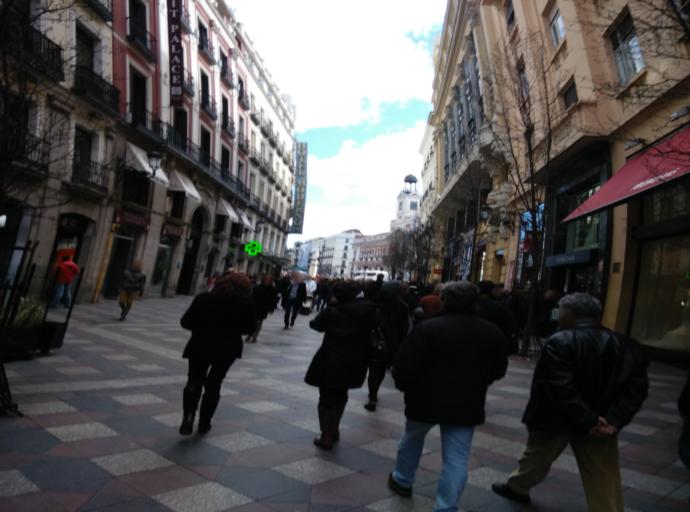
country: ES
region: Madrid
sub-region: Provincia de Madrid
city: Madrid
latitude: 40.4171
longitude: -3.7054
